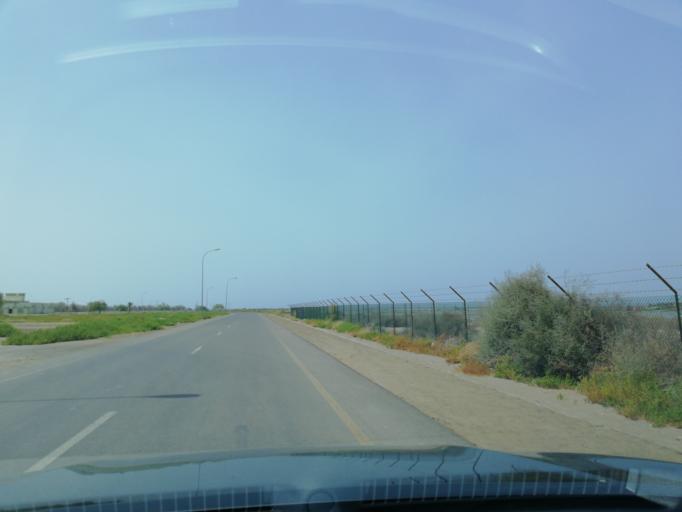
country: OM
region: Al Batinah
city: Shinas
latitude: 24.7512
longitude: 56.4674
